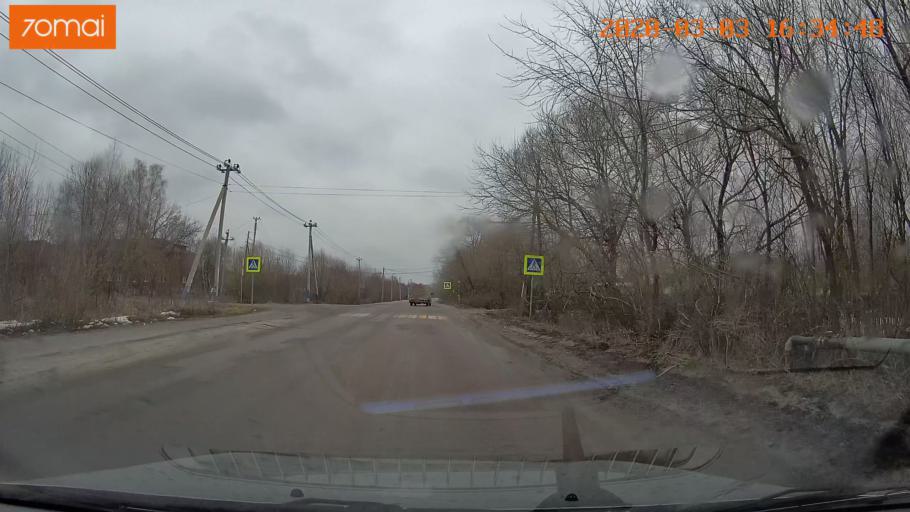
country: RU
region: Moskovskaya
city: Lopatinskiy
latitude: 55.4069
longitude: 38.7604
